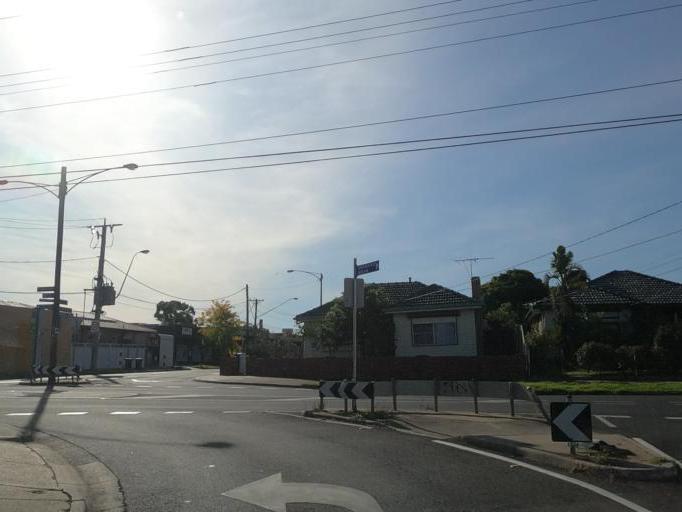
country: AU
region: Victoria
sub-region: Moonee Valley
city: Airport West
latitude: -37.7264
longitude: 144.8815
